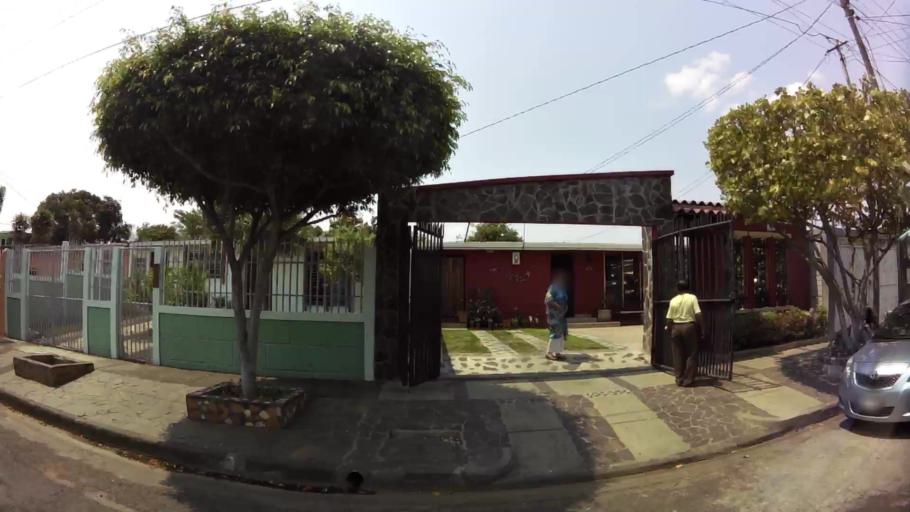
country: NI
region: Managua
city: Ciudad Sandino
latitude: 12.1513
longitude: -86.3133
